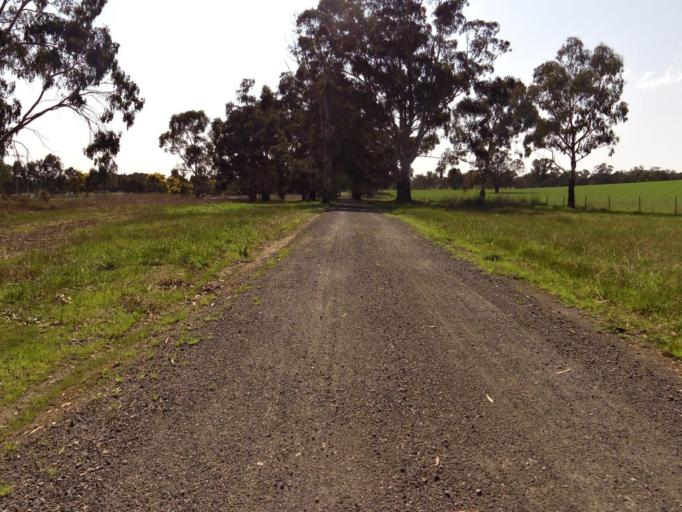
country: AU
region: Victoria
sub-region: Murrindindi
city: Alexandra
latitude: -37.1239
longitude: 145.5999
